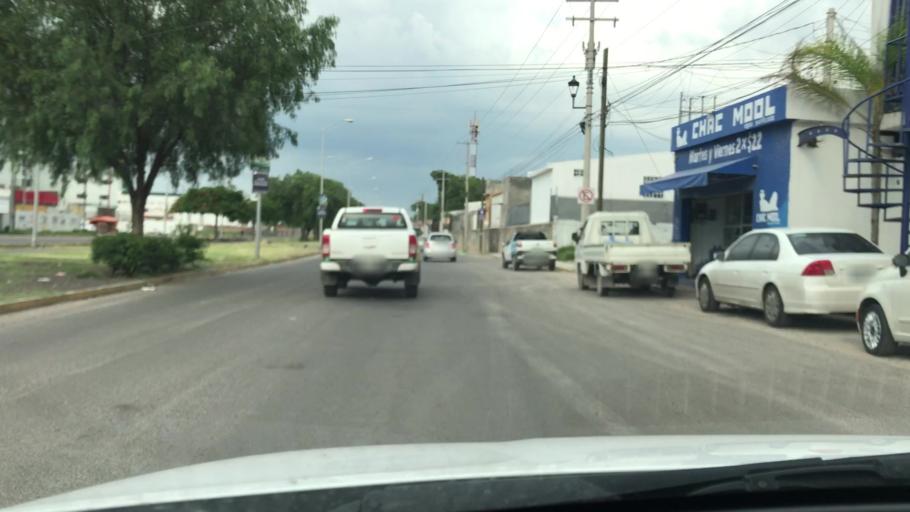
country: MX
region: Guanajuato
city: Celaya
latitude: 20.5363
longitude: -100.7963
